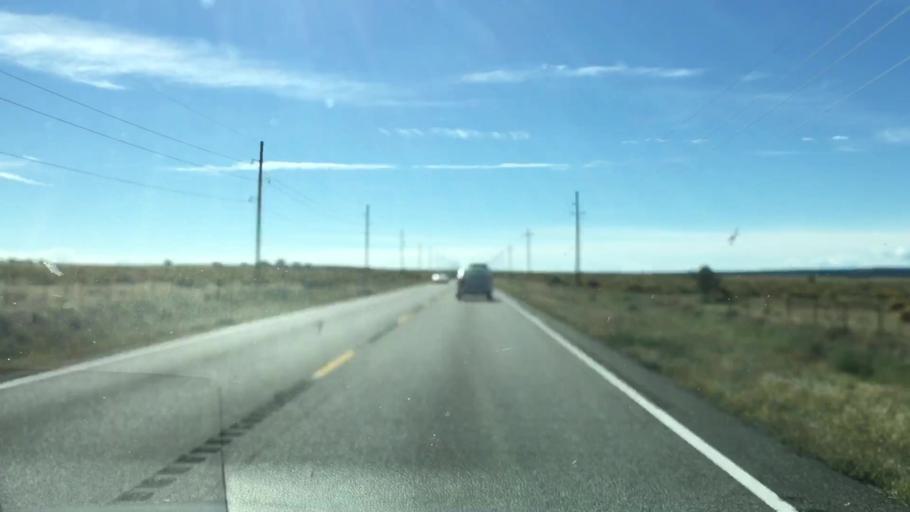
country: US
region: Arizona
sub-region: Mohave County
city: Colorado City
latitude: 37.0709
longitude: -113.1043
